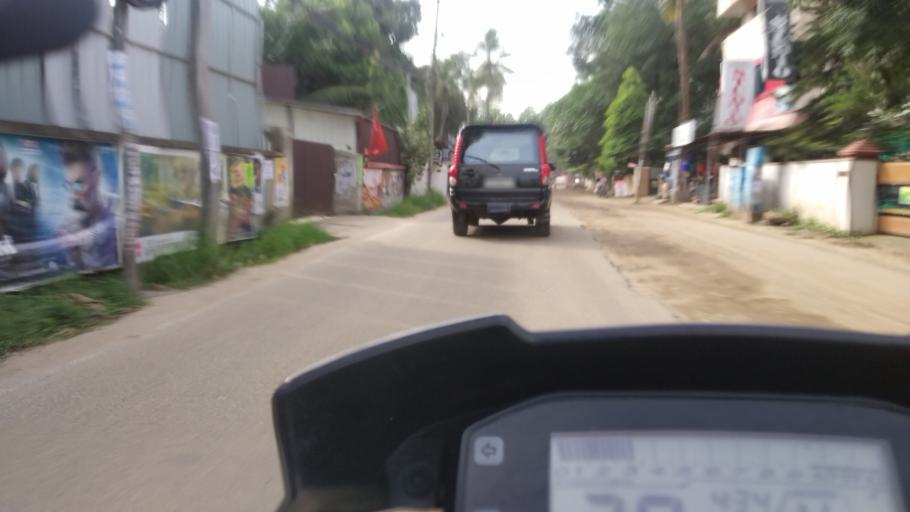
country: IN
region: Kerala
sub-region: Ernakulam
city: Cochin
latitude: 9.9813
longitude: 76.3132
